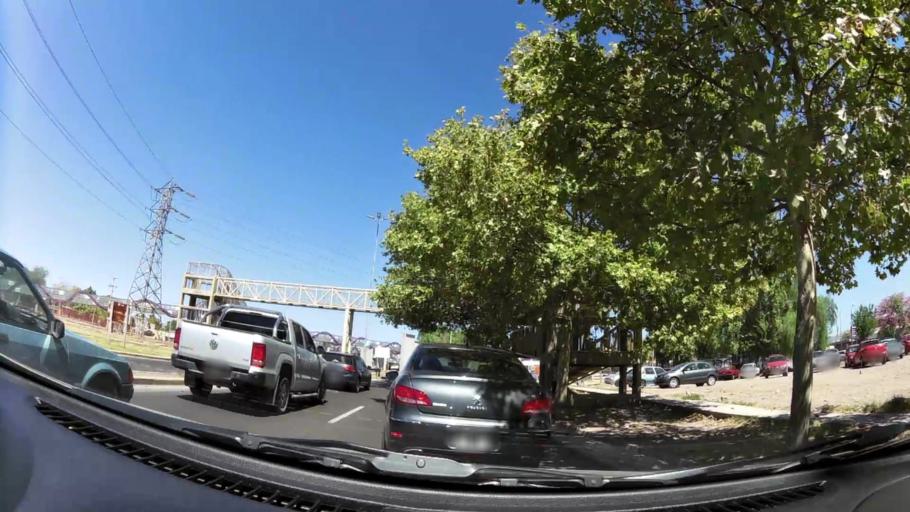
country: AR
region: Mendoza
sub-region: Departamento de Godoy Cruz
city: Godoy Cruz
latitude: -32.9228
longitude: -68.8638
